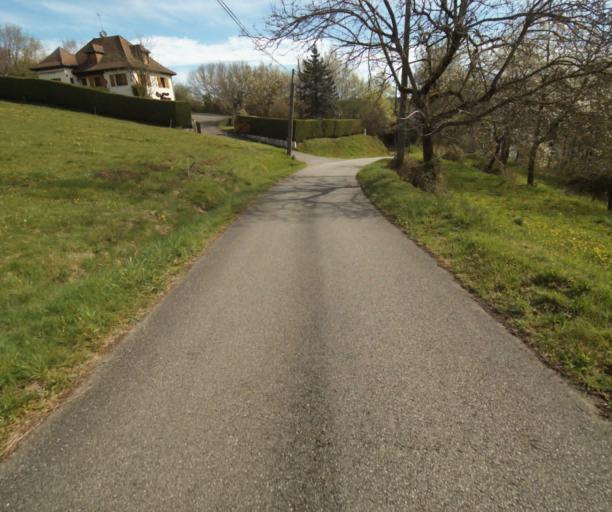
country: FR
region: Limousin
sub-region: Departement de la Correze
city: Laguenne
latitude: 45.2603
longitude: 1.8081
